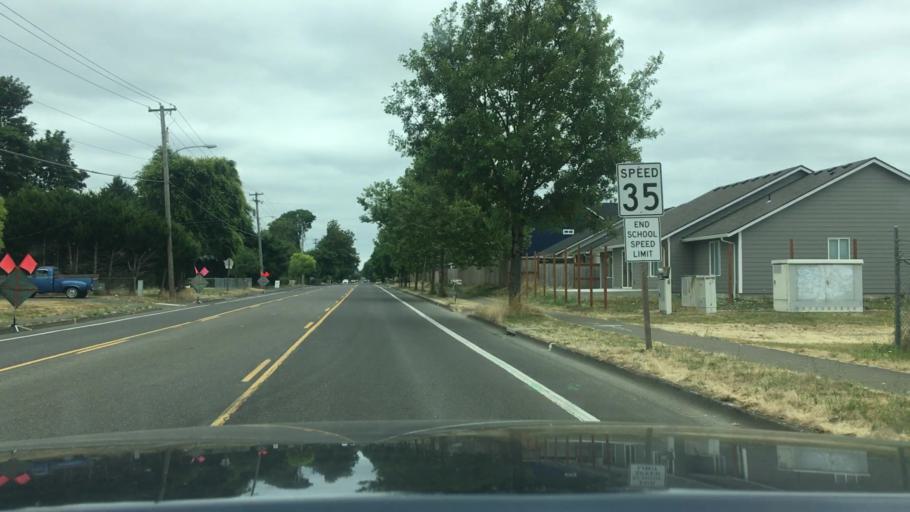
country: US
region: Oregon
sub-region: Lane County
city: Eugene
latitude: 44.0846
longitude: -123.1986
